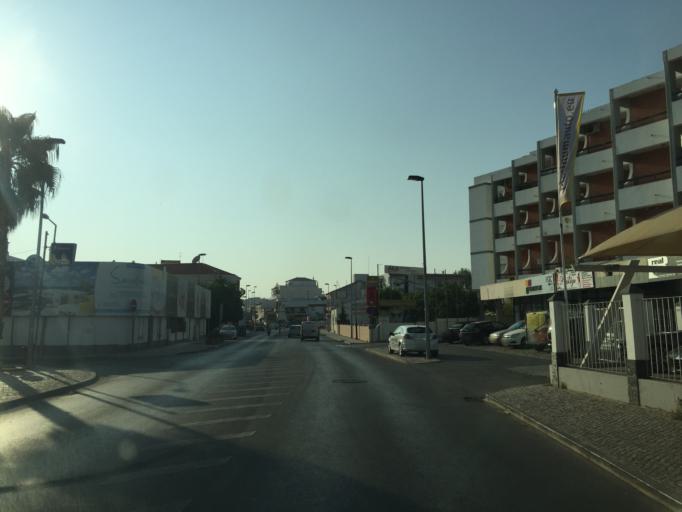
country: PT
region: Faro
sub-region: Loule
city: Almancil
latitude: 37.0860
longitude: -8.0287
